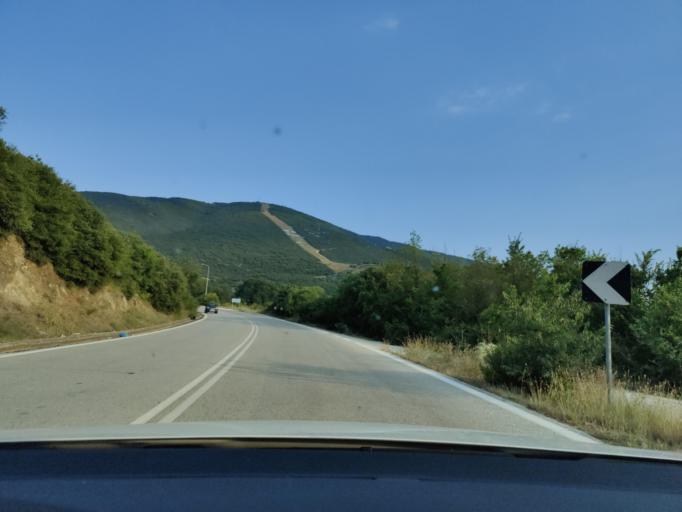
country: GR
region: East Macedonia and Thrace
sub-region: Nomos Kavalas
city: Zygos
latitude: 40.9986
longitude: 24.3805
